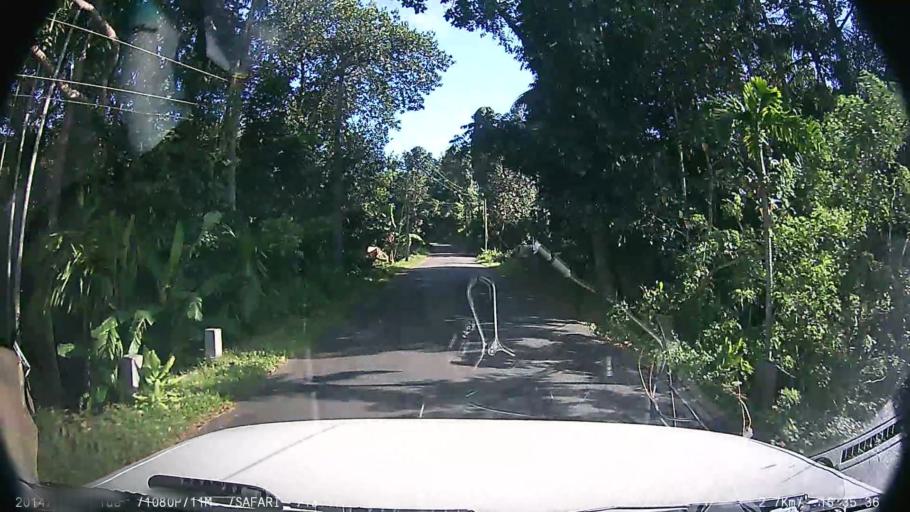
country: IN
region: Kerala
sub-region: Kottayam
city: Kottayam
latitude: 9.5450
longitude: 76.5378
